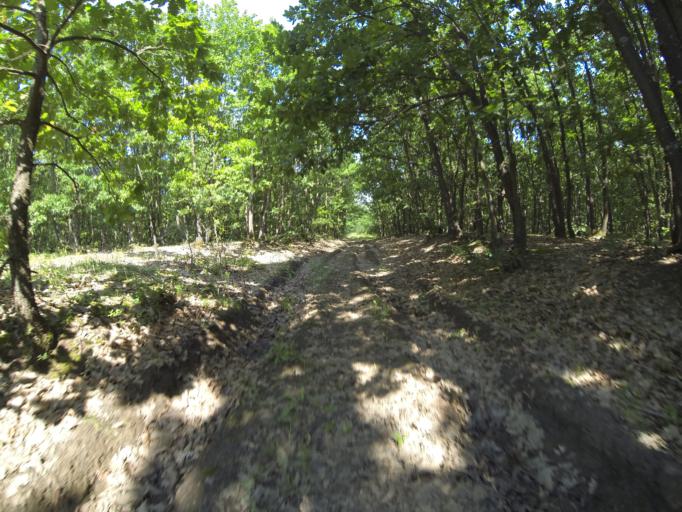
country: RO
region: Gorj
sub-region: Comuna Crusetu
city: Crusetu
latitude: 44.6134
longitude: 23.6424
